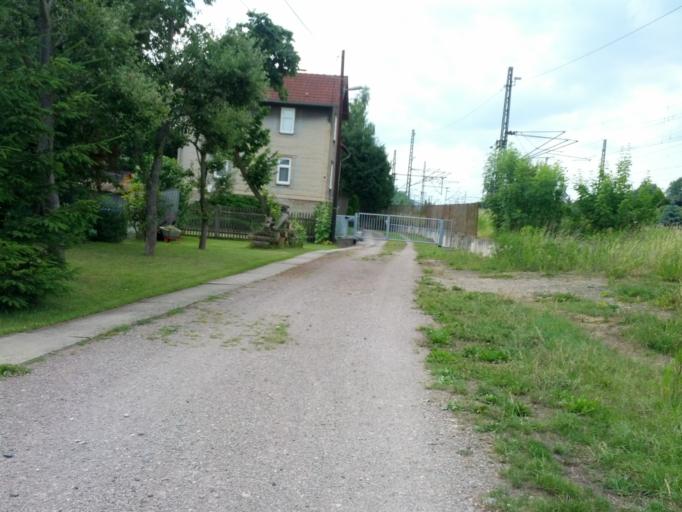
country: DE
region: Thuringia
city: Eisenach
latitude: 50.9672
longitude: 10.3542
